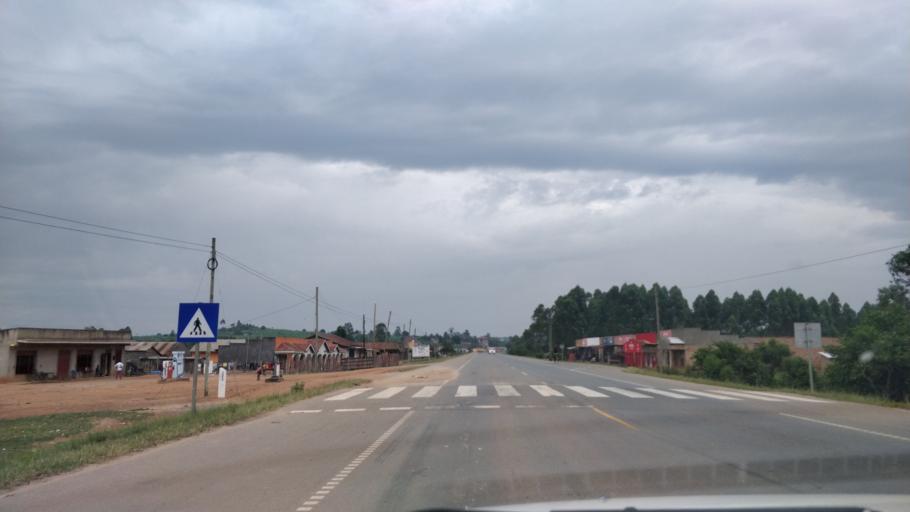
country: UG
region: Western Region
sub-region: Sheema District
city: Kibingo
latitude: -0.6636
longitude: 30.4512
